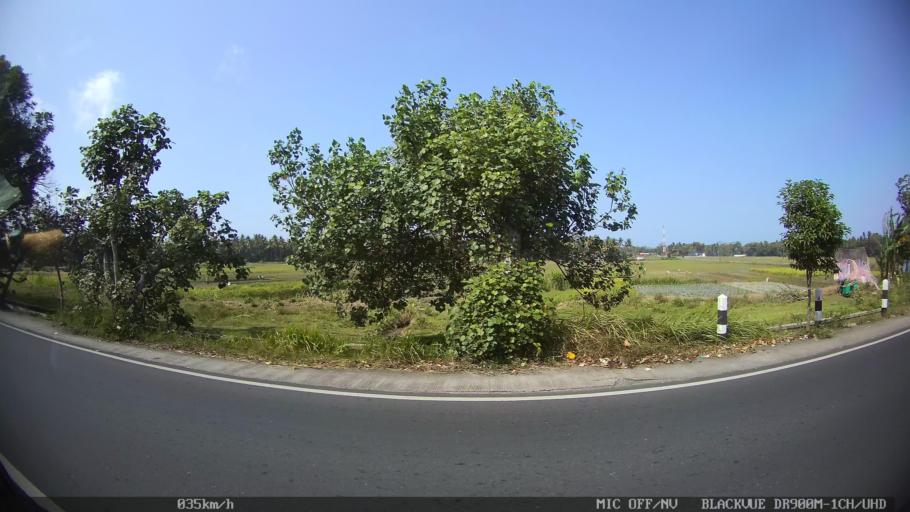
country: ID
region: Daerah Istimewa Yogyakarta
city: Srandakan
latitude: -7.9395
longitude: 110.2253
